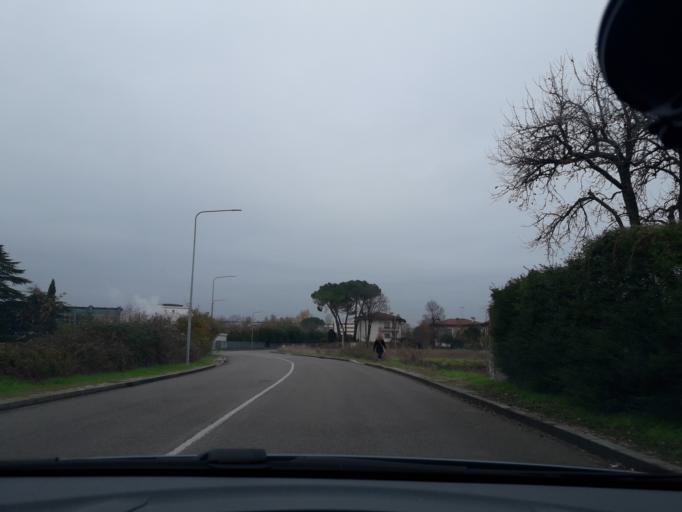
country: IT
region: Friuli Venezia Giulia
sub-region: Provincia di Udine
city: Colugna
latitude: 46.0755
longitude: 13.2166
